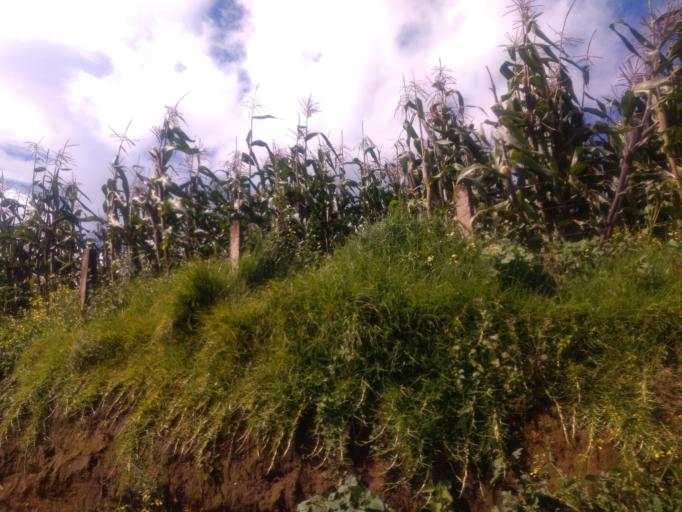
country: GT
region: Quetzaltenango
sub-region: Municipio de La Esperanza
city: La Esperanza
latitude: 14.8544
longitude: -91.5671
